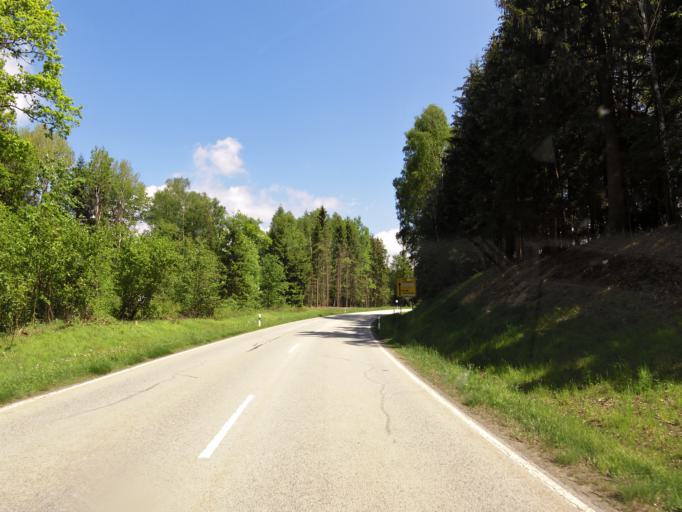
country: DE
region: Bavaria
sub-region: Lower Bavaria
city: Freyung
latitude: 48.8264
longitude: 13.5663
